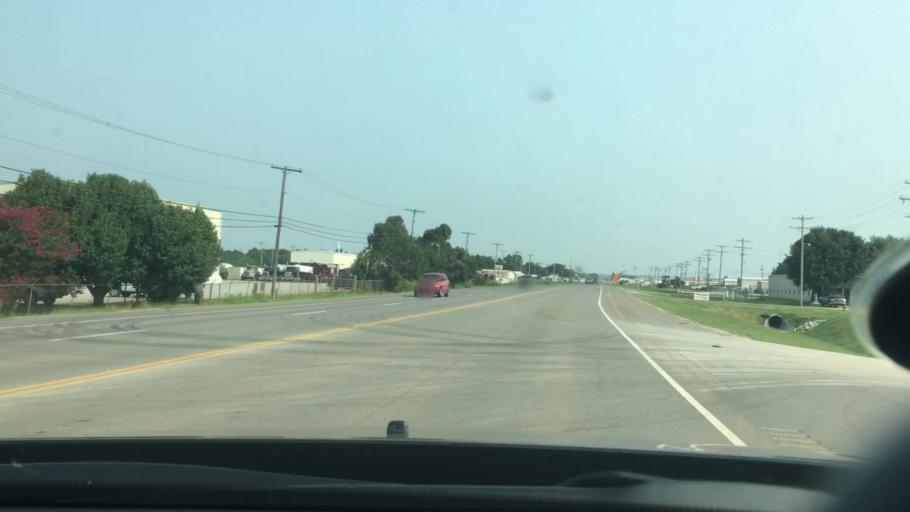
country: US
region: Oklahoma
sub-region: Garvin County
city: Lindsay
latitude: 34.8215
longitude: -97.5983
